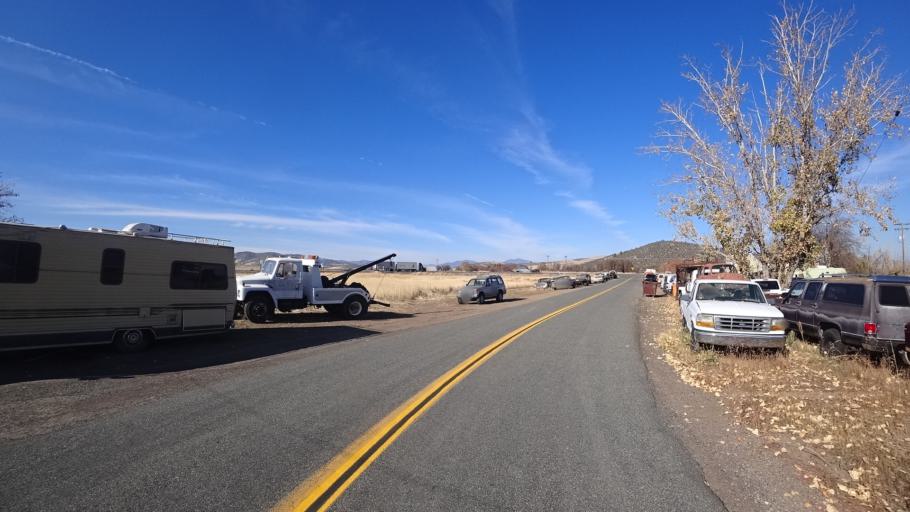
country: US
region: California
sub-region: Siskiyou County
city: Montague
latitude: 41.6456
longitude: -122.5321
